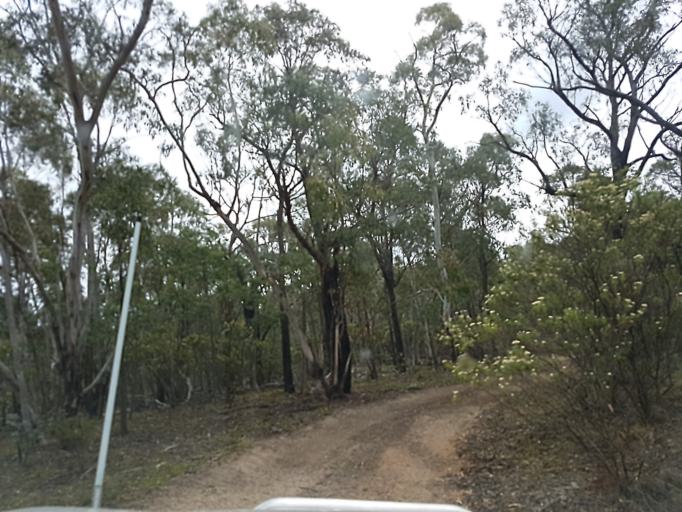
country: AU
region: New South Wales
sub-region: Snowy River
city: Jindabyne
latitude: -36.8902
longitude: 148.3376
